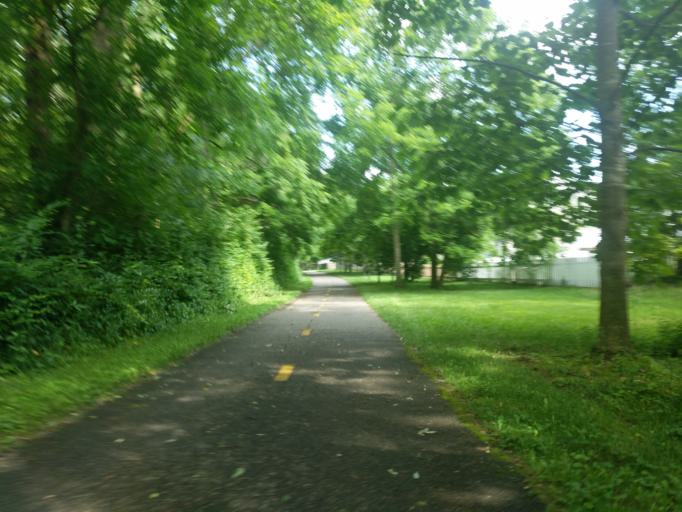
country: US
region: Ohio
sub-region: Franklin County
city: Huber Ridge
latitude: 40.0878
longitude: -82.9250
